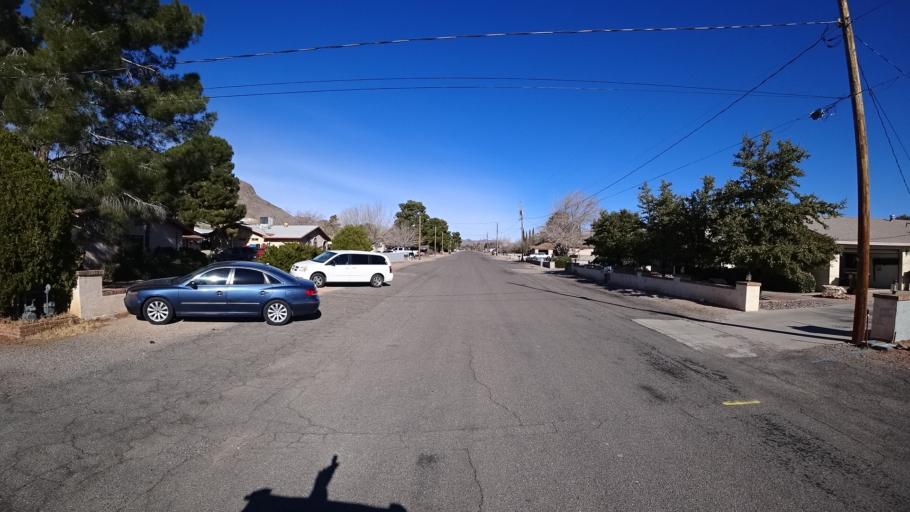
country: US
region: Arizona
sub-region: Mohave County
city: New Kingman-Butler
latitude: 35.2636
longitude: -114.0442
